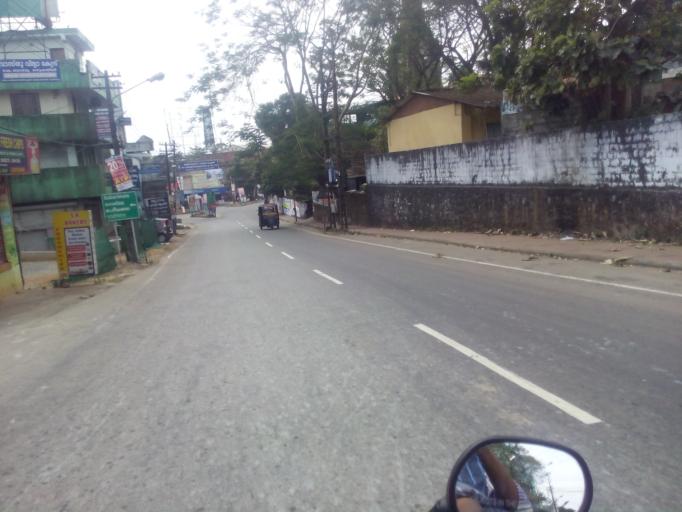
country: IN
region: Kerala
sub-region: Kottayam
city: Lalam
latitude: 9.7140
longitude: 76.6835
